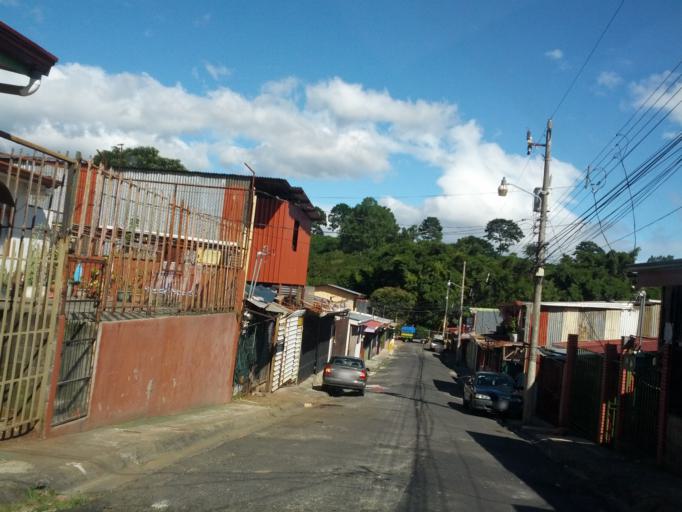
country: CR
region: Alajuela
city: Alajuela
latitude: 10.0248
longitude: -84.1999
